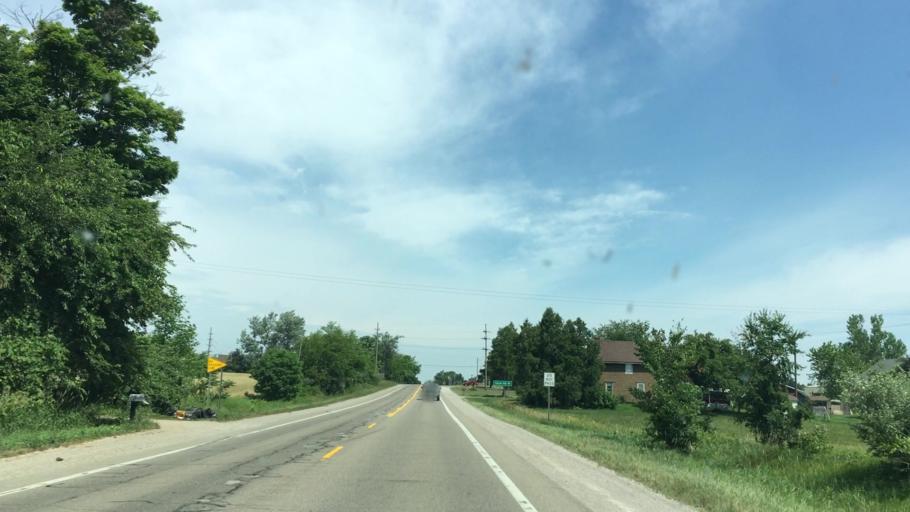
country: US
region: Michigan
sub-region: Lapeer County
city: Imlay City
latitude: 43.0997
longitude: -83.0718
